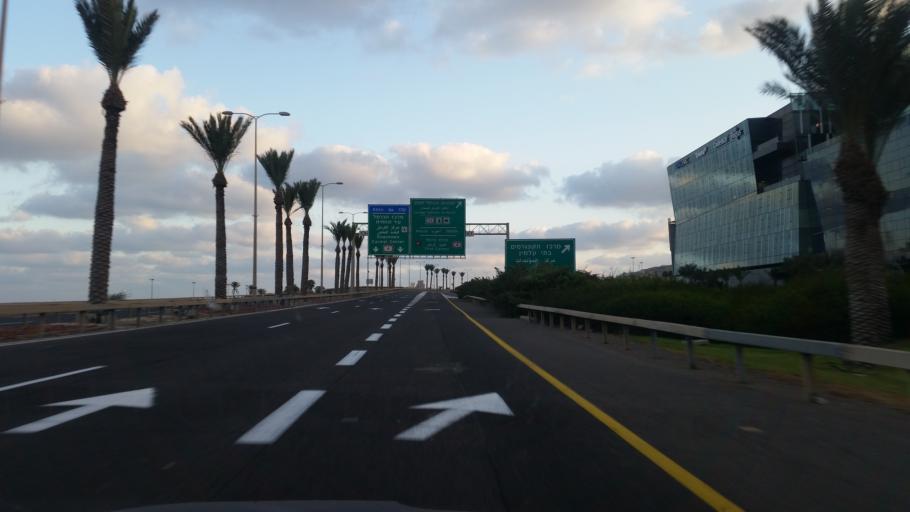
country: IL
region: Haifa
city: Tirat Karmel
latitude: 32.7871
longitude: 34.9567
